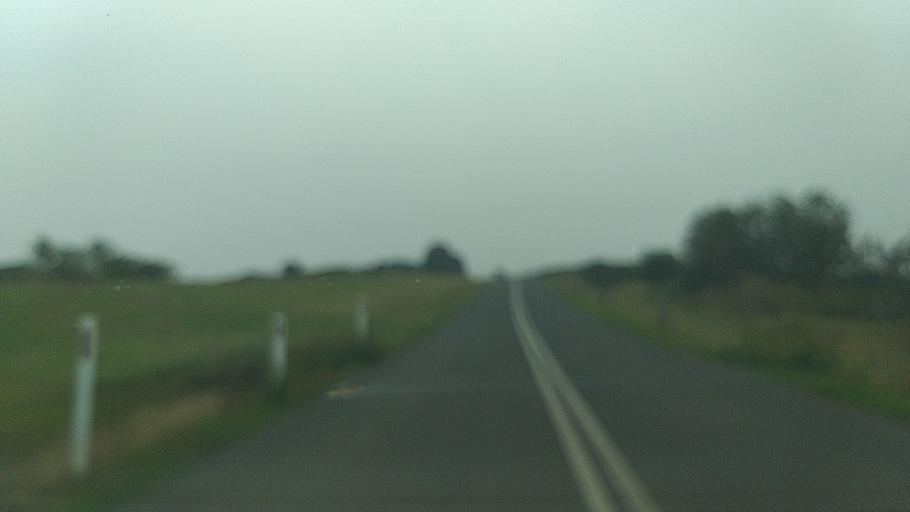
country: AU
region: New South Wales
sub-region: Shellharbour
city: Croom
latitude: -34.6095
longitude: 150.8596
